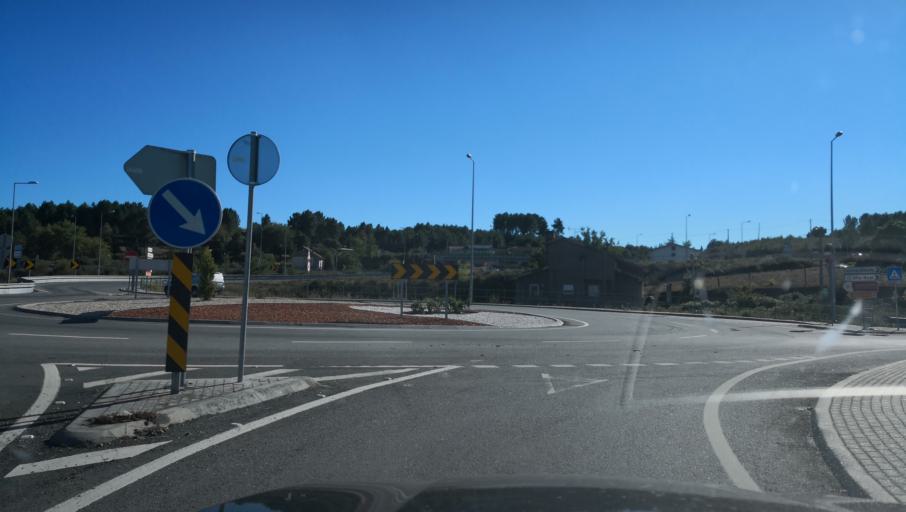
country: PT
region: Vila Real
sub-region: Vila Real
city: Vila Real
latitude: 41.2822
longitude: -7.7208
